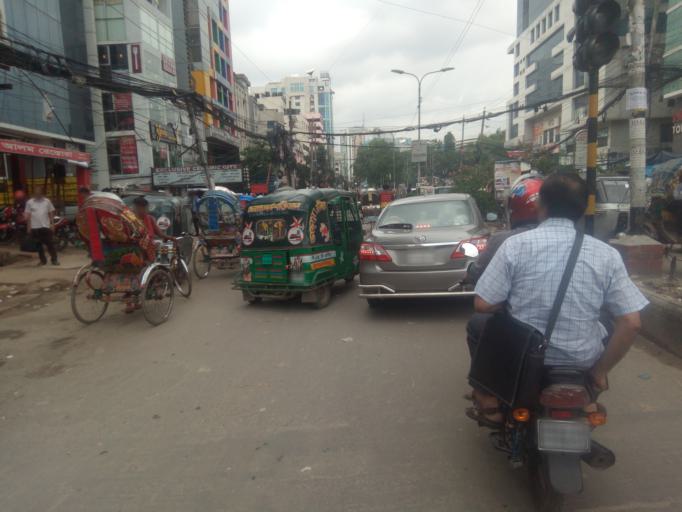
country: BD
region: Dhaka
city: Azimpur
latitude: 23.7460
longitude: 90.3926
